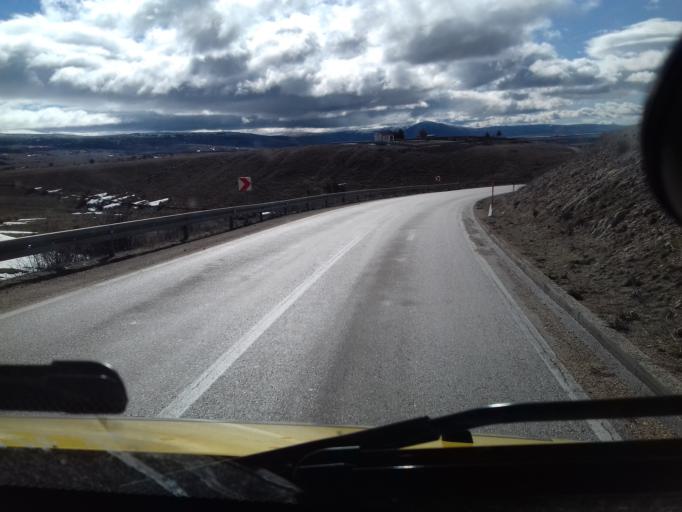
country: BA
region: Federation of Bosnia and Herzegovina
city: Tomislavgrad
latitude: 43.7660
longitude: 17.2378
